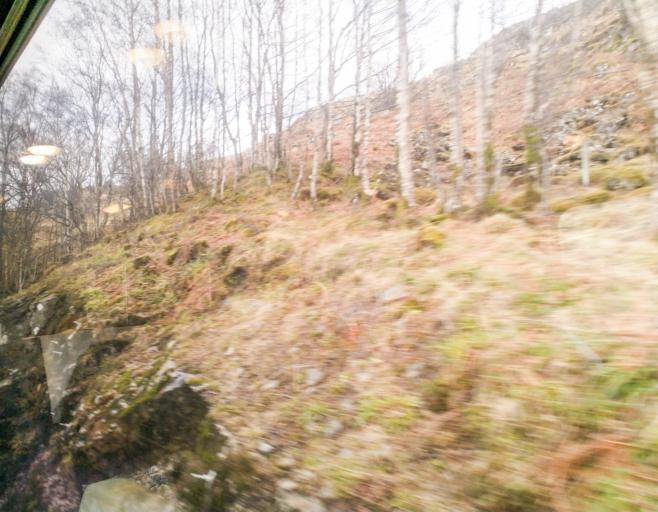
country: GB
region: Scotland
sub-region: Highland
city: Spean Bridge
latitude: 56.7934
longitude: -4.7255
